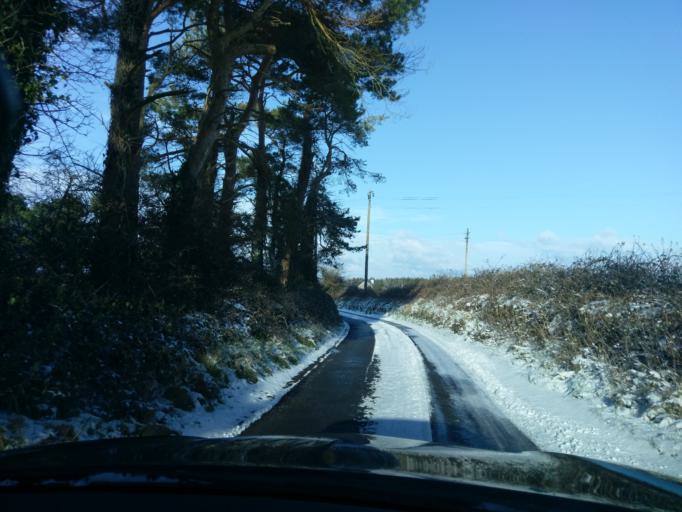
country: IE
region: Connaught
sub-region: County Galway
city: Oranmore
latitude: 53.1928
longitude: -8.8402
